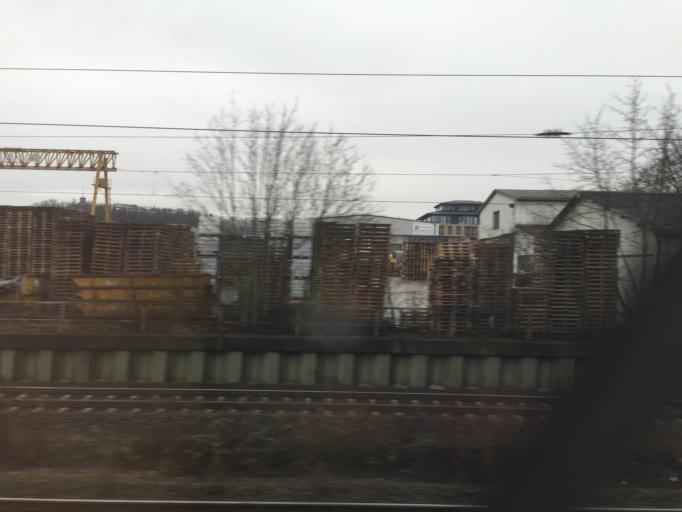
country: DE
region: Baden-Wuerttemberg
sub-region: Regierungsbezirk Stuttgart
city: Asperg
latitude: 48.9201
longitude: 9.1360
